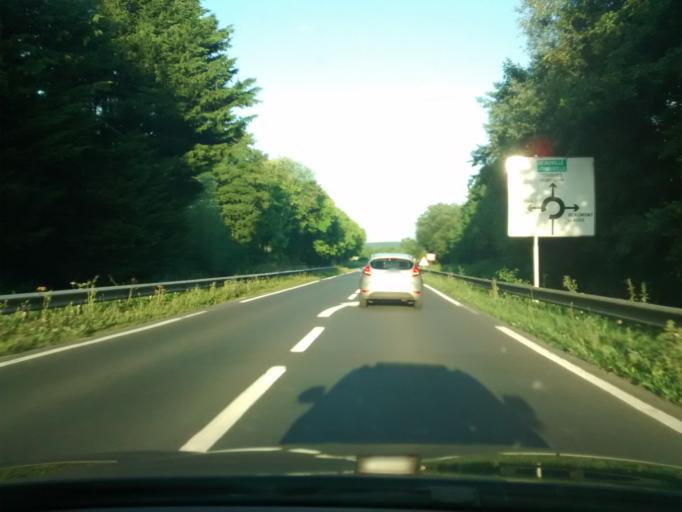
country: FR
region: Lower Normandy
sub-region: Departement du Calvados
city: Touques
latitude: 49.3277
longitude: 0.0825
